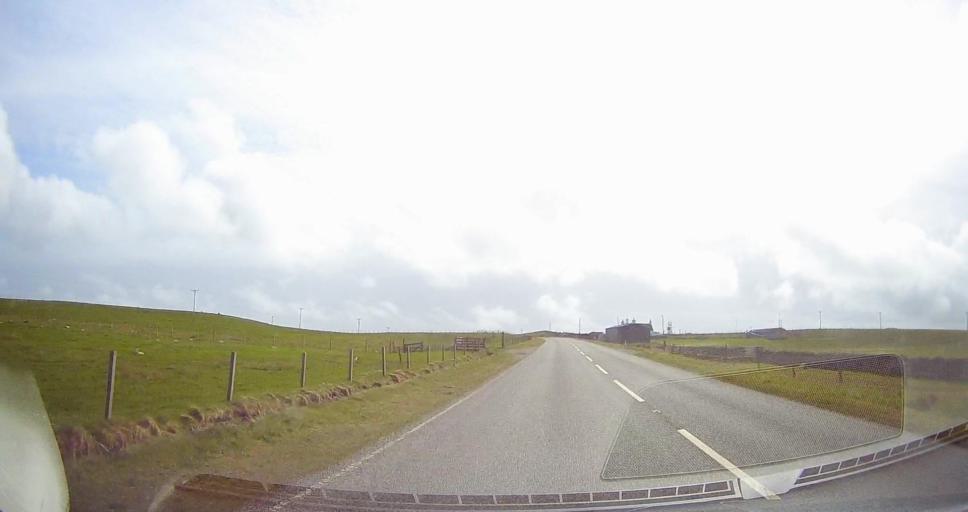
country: GB
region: Scotland
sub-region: Shetland Islands
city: Sandwick
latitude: 59.9154
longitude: -1.3009
